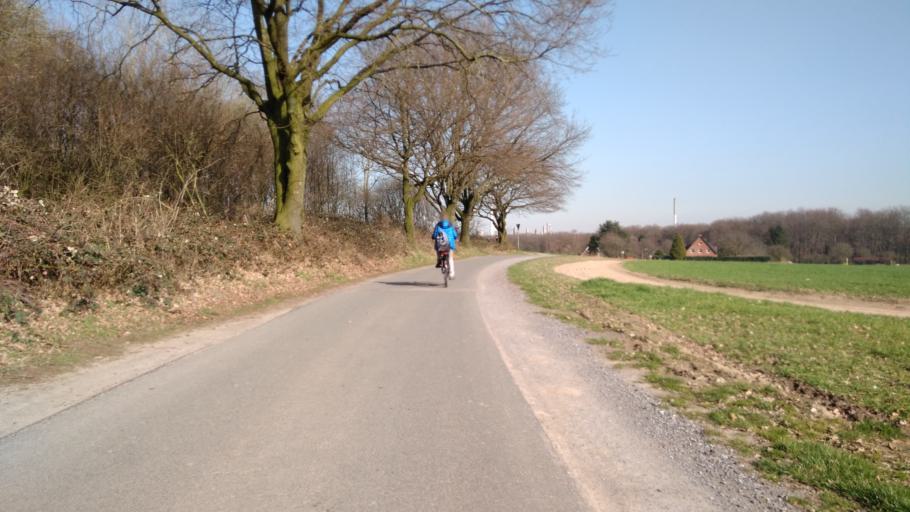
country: DE
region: North Rhine-Westphalia
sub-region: Regierungsbezirk Munster
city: Gladbeck
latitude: 51.5975
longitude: 6.9481
